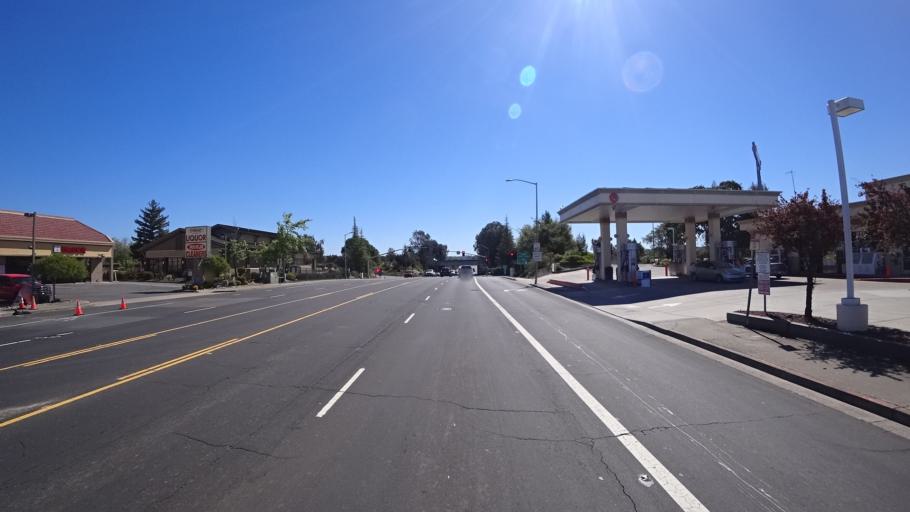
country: US
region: California
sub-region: Placer County
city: Rocklin
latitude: 38.7884
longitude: -121.2250
